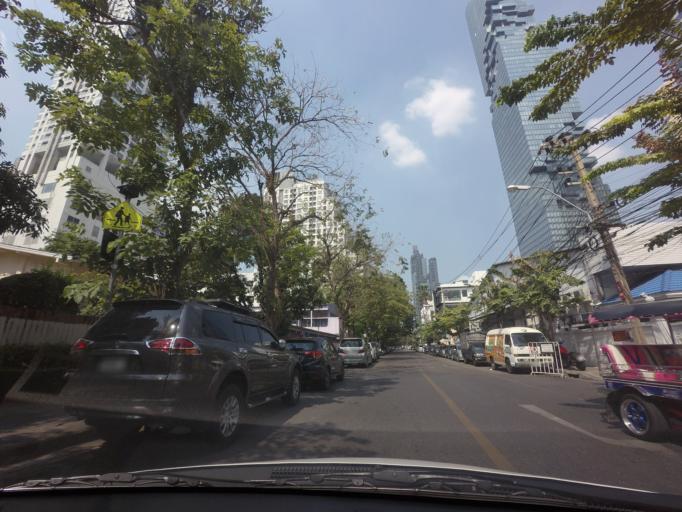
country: TH
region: Bangkok
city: Bang Rak
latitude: 13.7215
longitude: 100.5278
